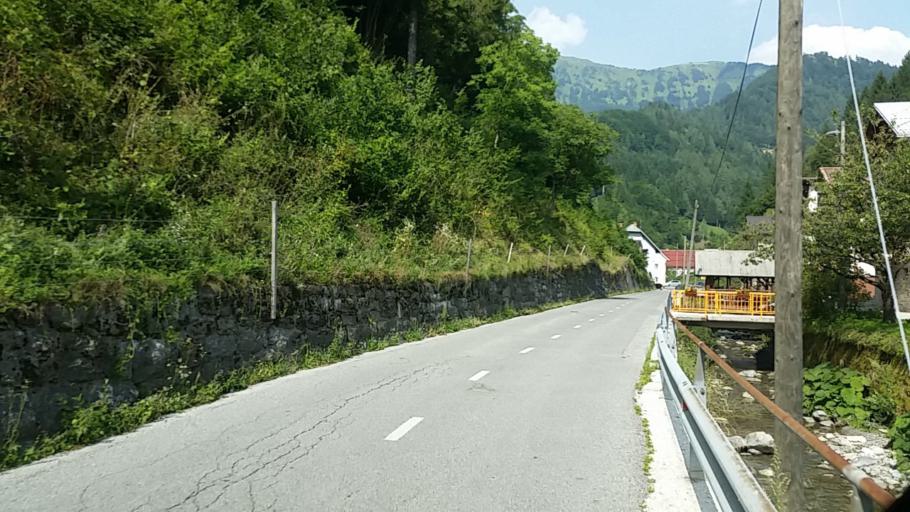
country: SI
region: Bohinj
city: Bohinjska Bistrica
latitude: 46.2122
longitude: 13.9698
